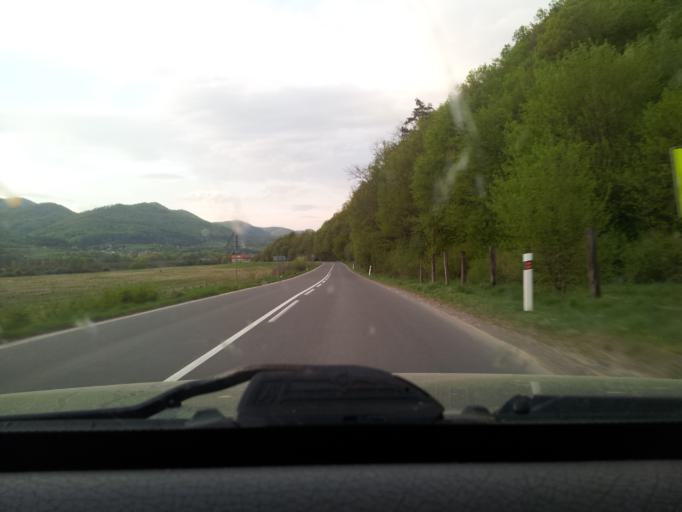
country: SK
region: Banskobystricky
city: Zarnovica
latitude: 48.5176
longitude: 18.7400
